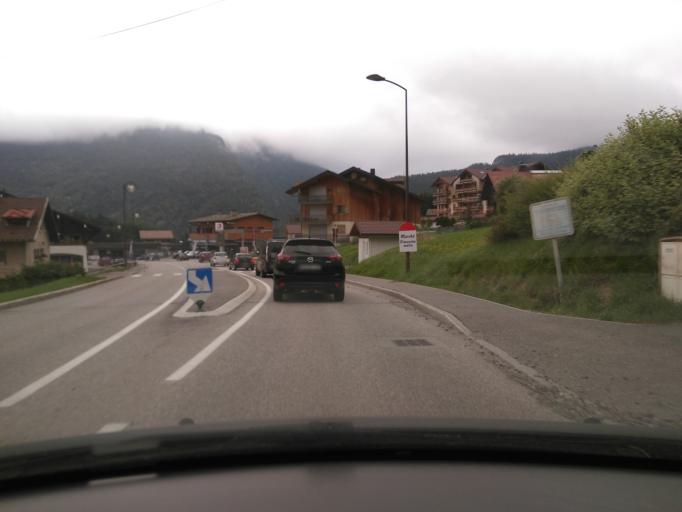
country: FR
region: Rhone-Alpes
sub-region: Departement de la Haute-Savoie
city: Saint-Jean-de-Sixt
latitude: 45.9229
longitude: 6.4142
